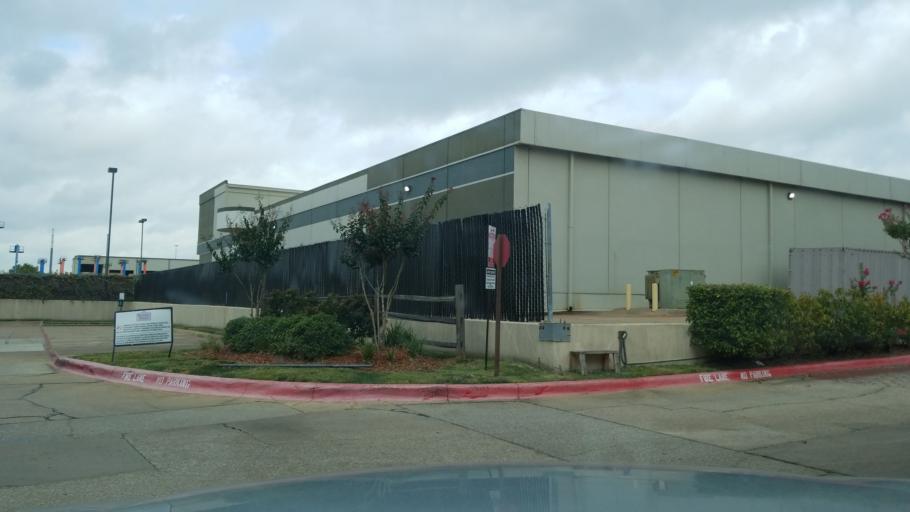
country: US
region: Texas
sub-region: Tarrant County
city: Euless
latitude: 32.8361
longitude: -97.1127
